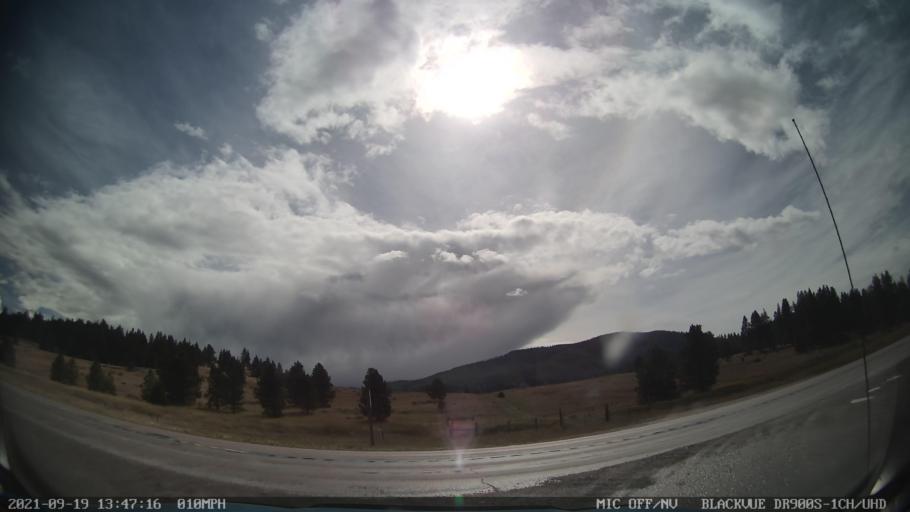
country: US
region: Montana
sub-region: Missoula County
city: Seeley Lake
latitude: 47.0314
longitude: -113.2608
